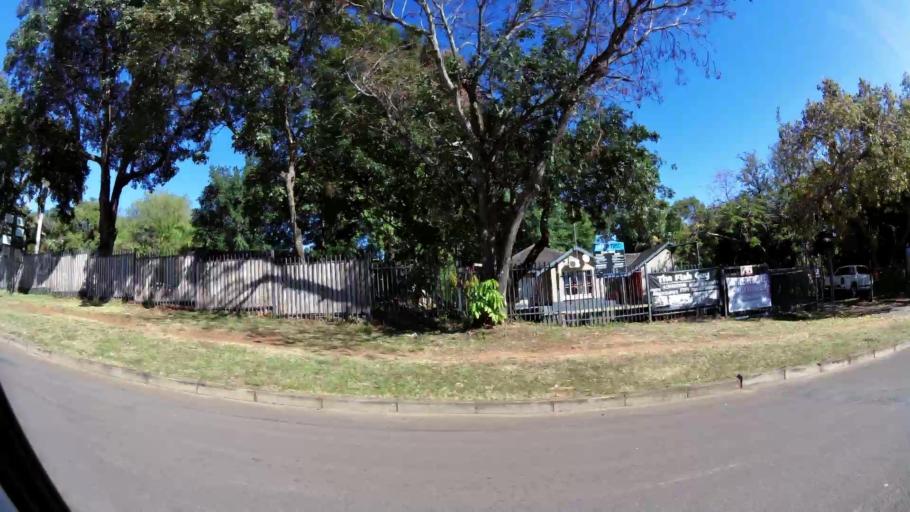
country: ZA
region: Limpopo
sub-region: Mopani District Municipality
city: Tzaneen
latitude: -23.8313
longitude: 30.1519
